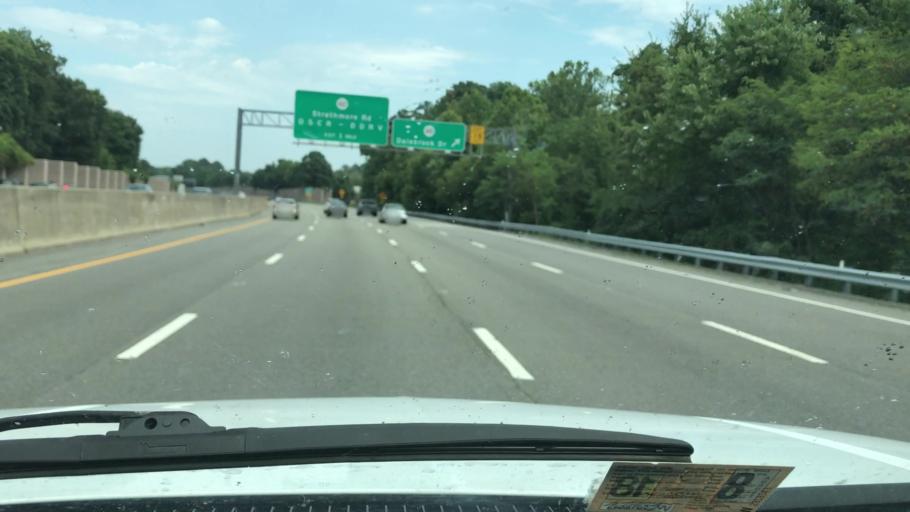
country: US
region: Virginia
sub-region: Chesterfield County
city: Bensley
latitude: 37.4393
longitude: -77.4667
